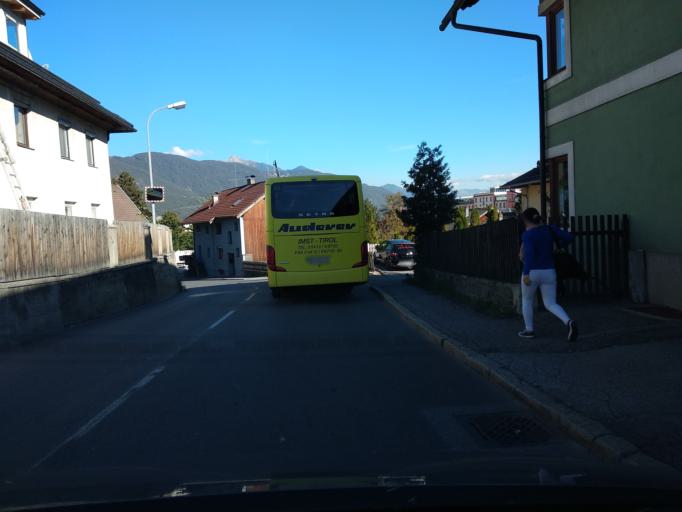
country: AT
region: Tyrol
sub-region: Politischer Bezirk Innsbruck Land
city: Telfs
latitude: 47.3101
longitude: 11.0637
